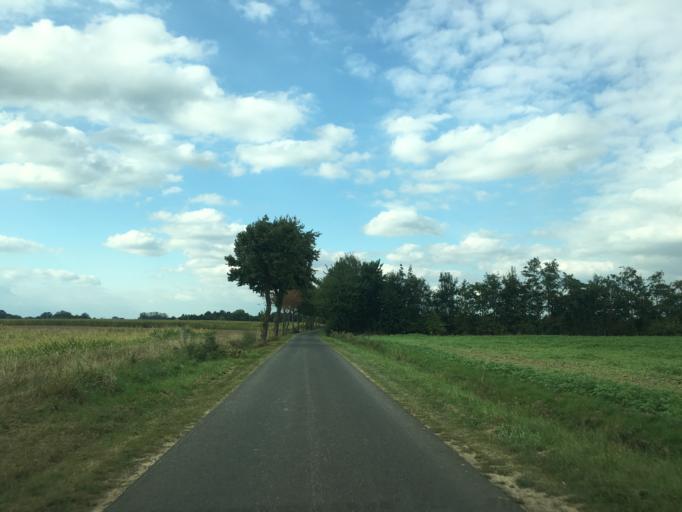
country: DE
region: North Rhine-Westphalia
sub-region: Regierungsbezirk Munster
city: Muenster
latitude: 51.9766
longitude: 7.5326
